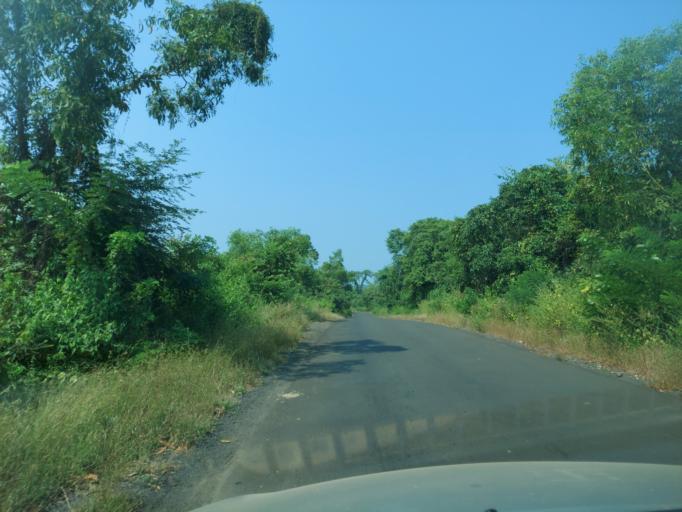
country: IN
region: Maharashtra
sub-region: Sindhudurg
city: Kudal
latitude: 15.9759
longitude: 73.6199
